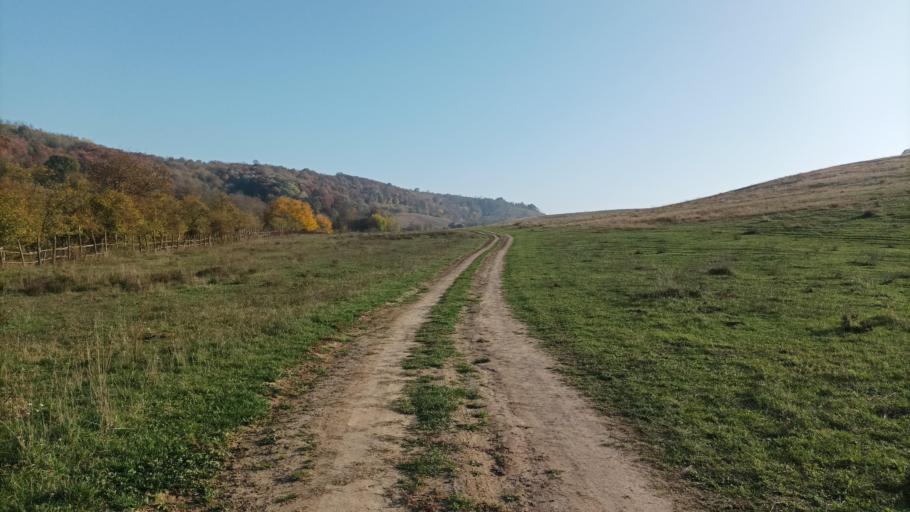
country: HU
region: Tolna
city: Szentgalpuszta
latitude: 46.3387
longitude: 18.6038
